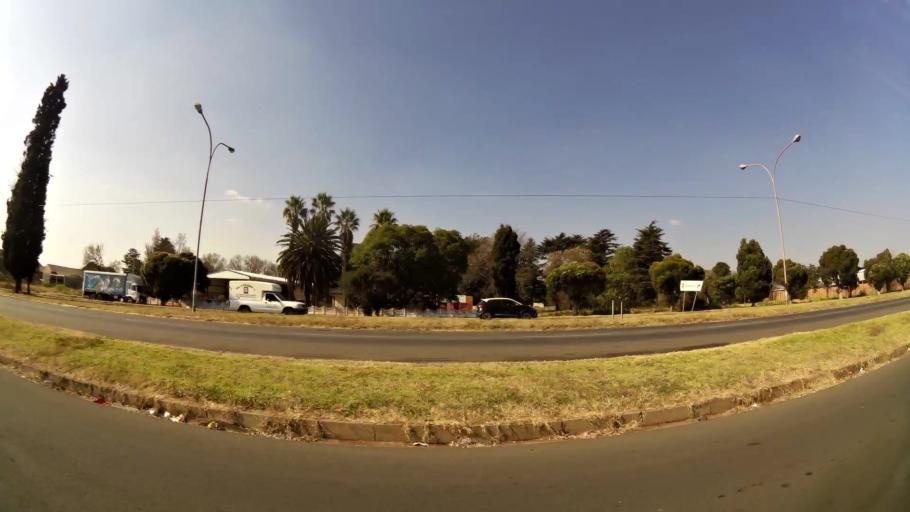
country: ZA
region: Gauteng
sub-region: City of Johannesburg Metropolitan Municipality
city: Modderfontein
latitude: -26.1222
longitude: 28.2288
